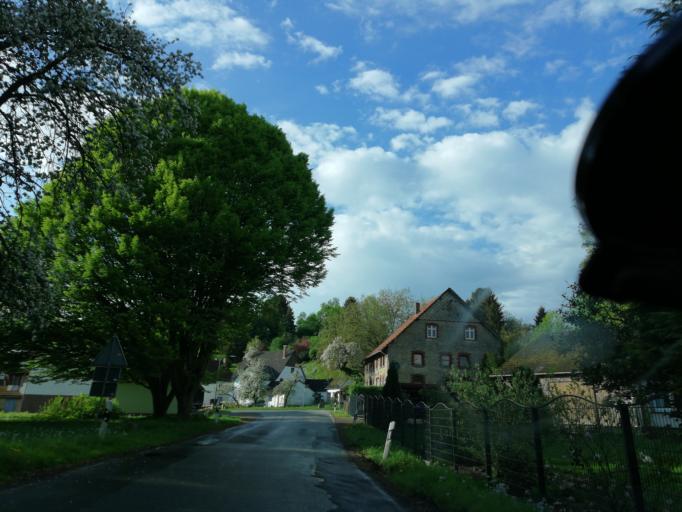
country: DE
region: North Rhine-Westphalia
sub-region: Regierungsbezirk Detmold
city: Dorentrup
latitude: 52.1252
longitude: 8.9988
